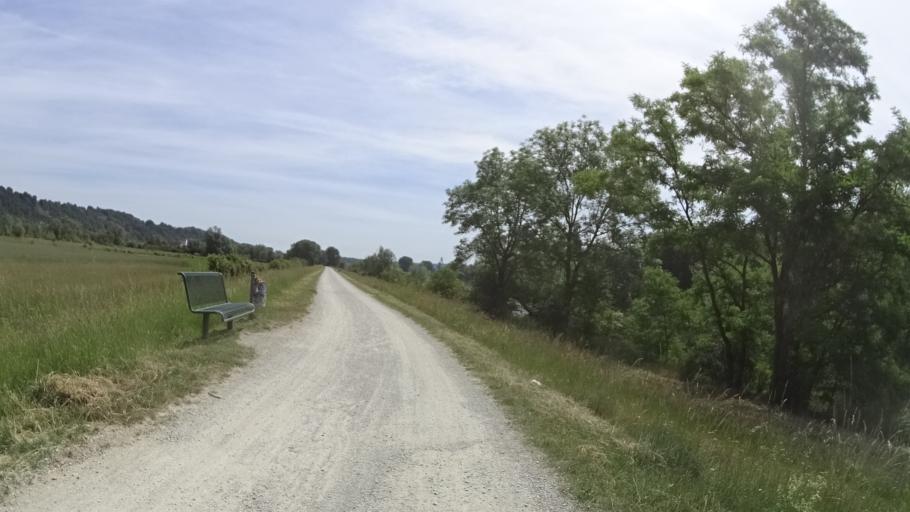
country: DE
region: Bavaria
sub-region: Lower Bavaria
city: Kelheim
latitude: 48.9106
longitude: 11.8999
